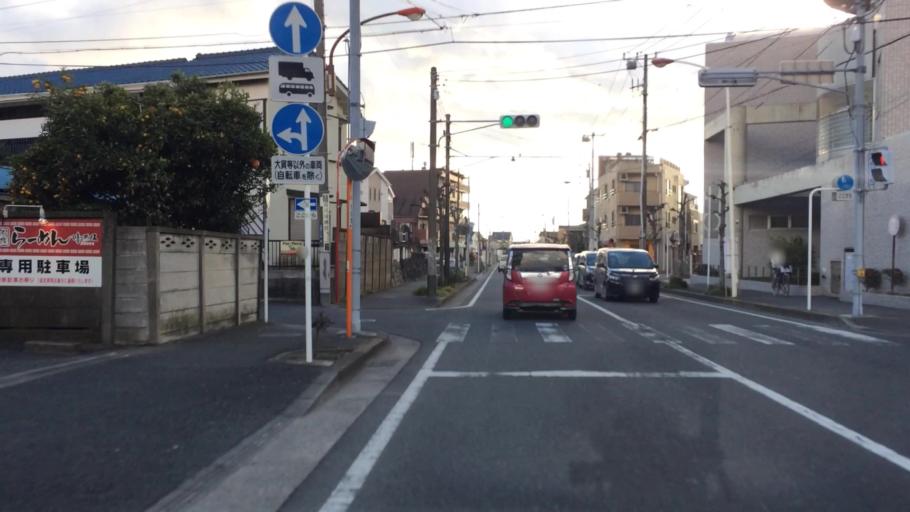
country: JP
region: Kanagawa
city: Fujisawa
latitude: 35.3344
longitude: 139.4725
